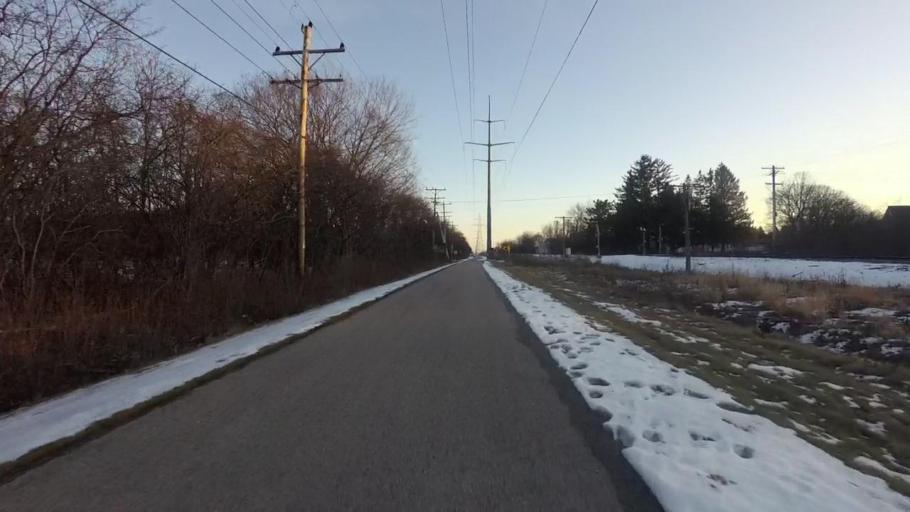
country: US
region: Wisconsin
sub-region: Milwaukee County
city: Brown Deer
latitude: 43.1566
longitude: -87.9579
